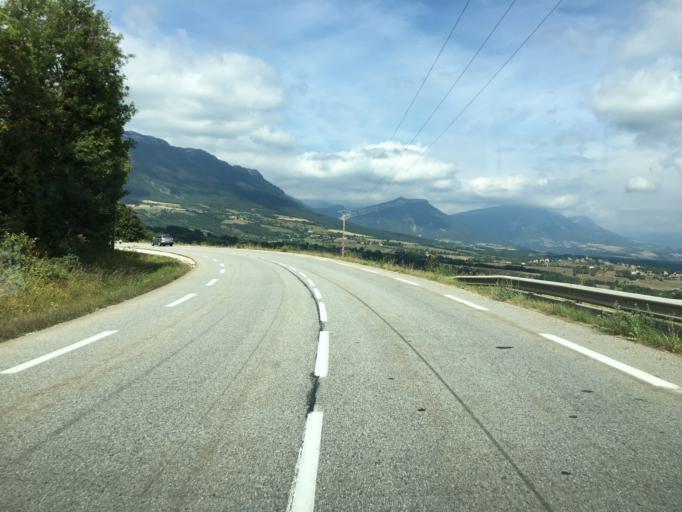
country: FR
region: Rhone-Alpes
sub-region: Departement de l'Isere
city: Mens
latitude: 44.7767
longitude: 5.6601
